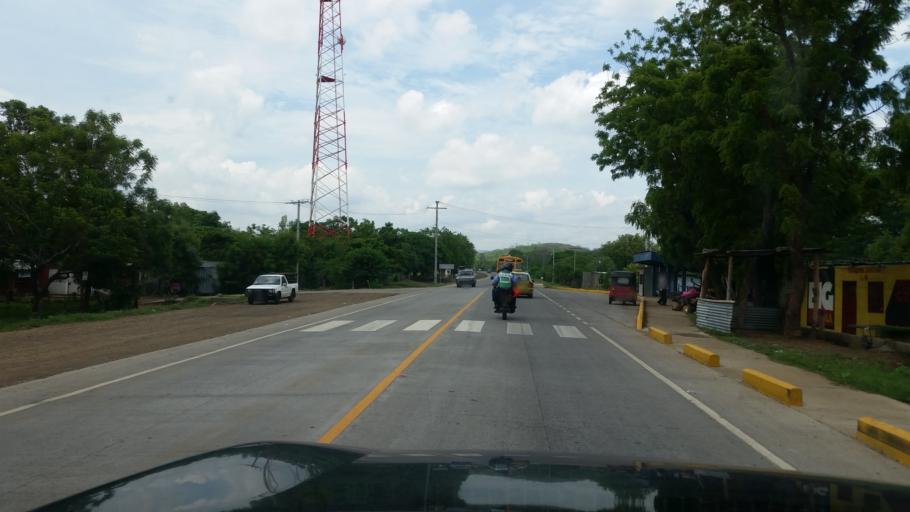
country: NI
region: Managua
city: Carlos Fonseca Amador
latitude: 12.0650
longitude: -86.4730
